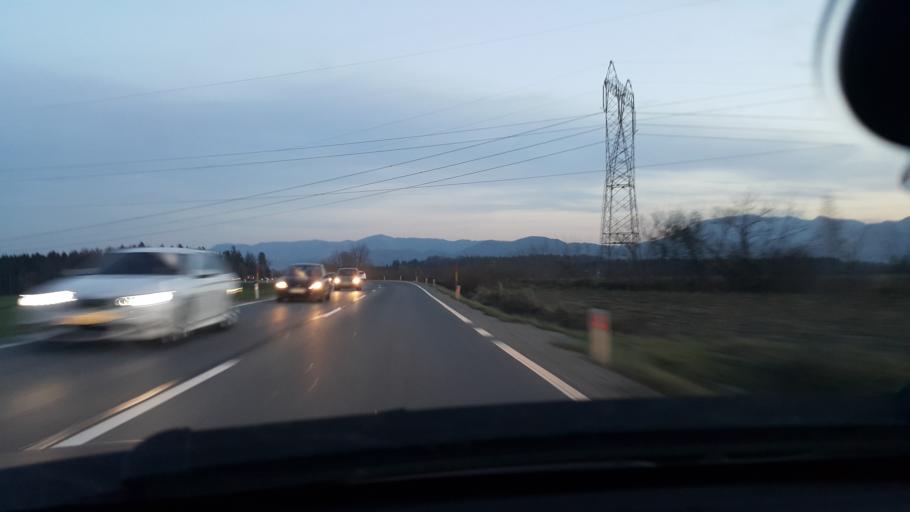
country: SI
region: Zalec
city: Gotovlje
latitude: 46.2803
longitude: 15.1818
